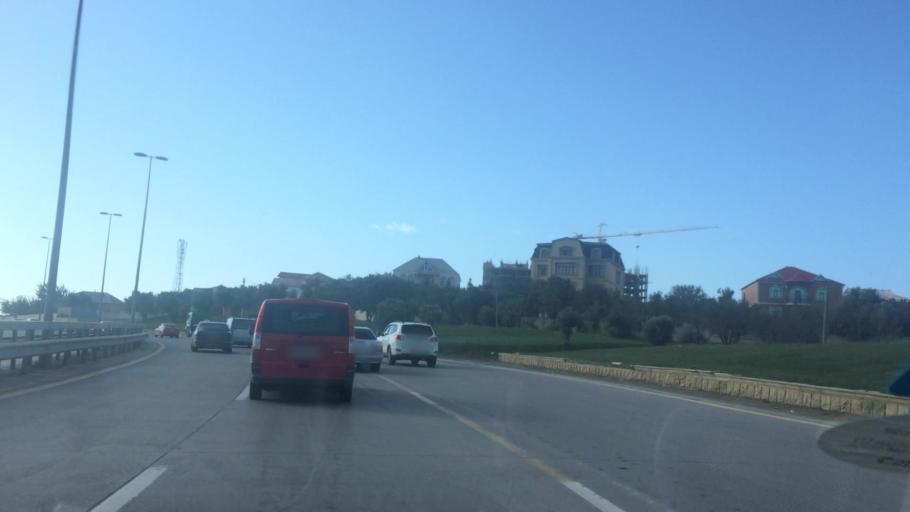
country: AZ
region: Baki
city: Qaracuxur
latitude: 40.3485
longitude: 49.9655
